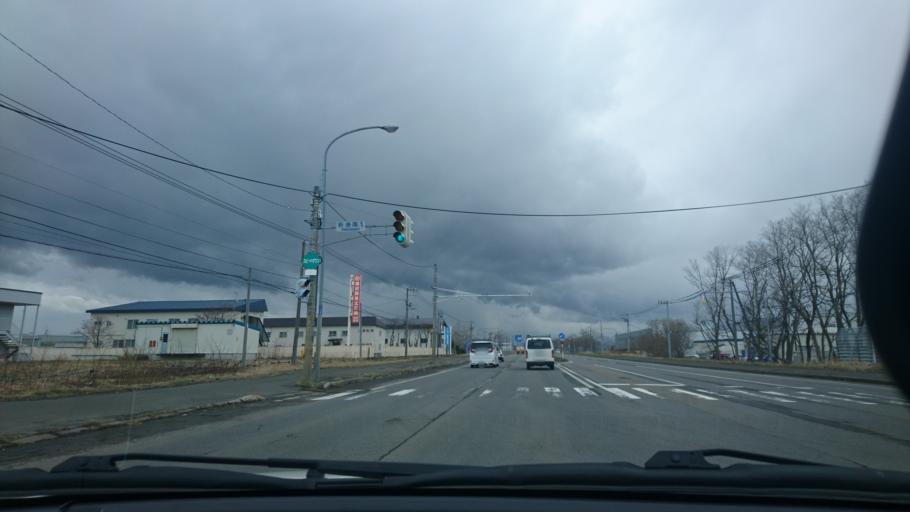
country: JP
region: Hokkaido
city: Ishikari
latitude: 43.1985
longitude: 141.3293
